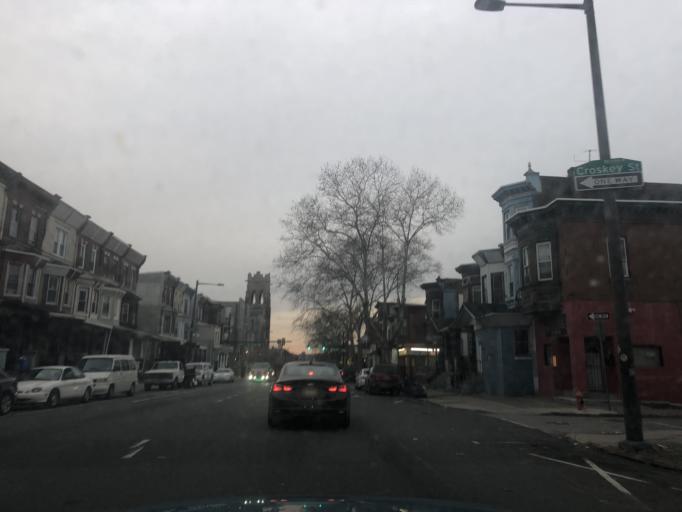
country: US
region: Pennsylvania
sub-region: Philadelphia County
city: Philadelphia
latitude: 39.9957
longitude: -75.1679
